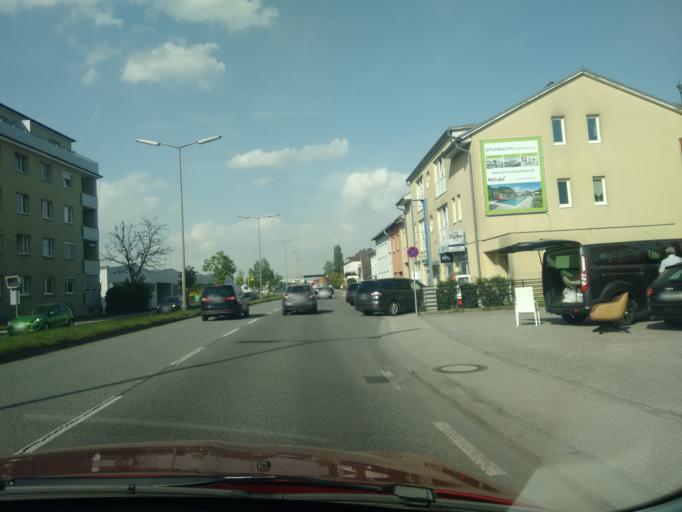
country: AT
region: Upper Austria
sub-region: Wels Stadt
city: Wels
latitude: 48.1735
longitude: 14.0538
